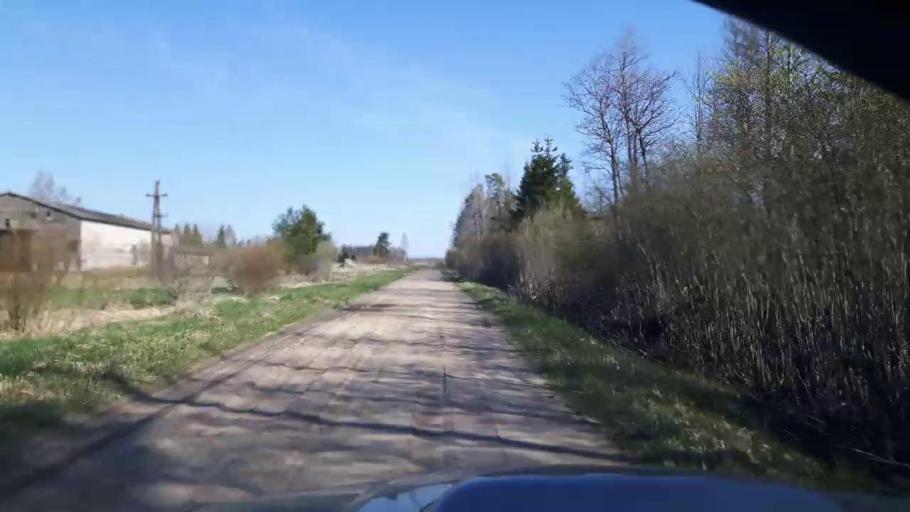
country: EE
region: Paernumaa
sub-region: Vaendra vald (alev)
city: Vandra
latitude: 58.5178
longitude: 24.9606
